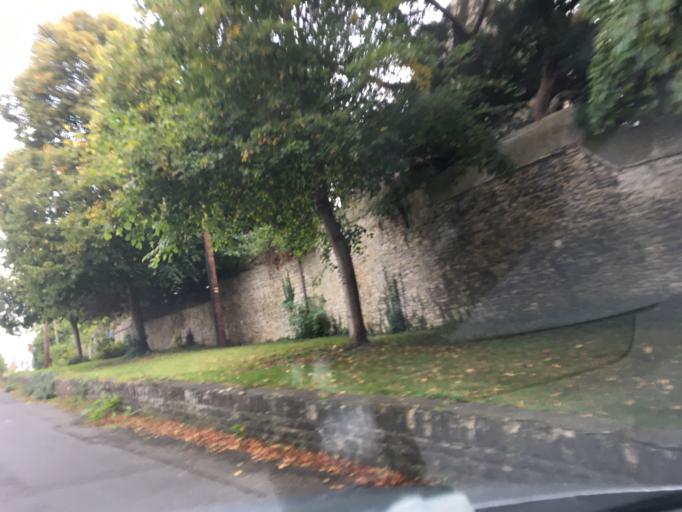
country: GB
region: England
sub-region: Oxfordshire
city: Kidlington
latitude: 51.8219
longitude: -1.2366
